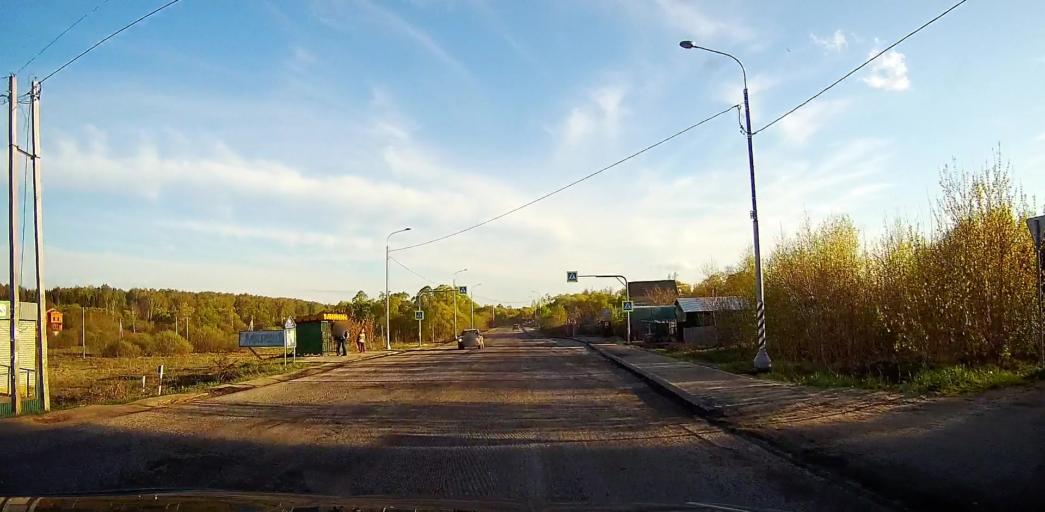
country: RU
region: Moskovskaya
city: Bronnitsy
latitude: 55.3086
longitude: 38.2135
